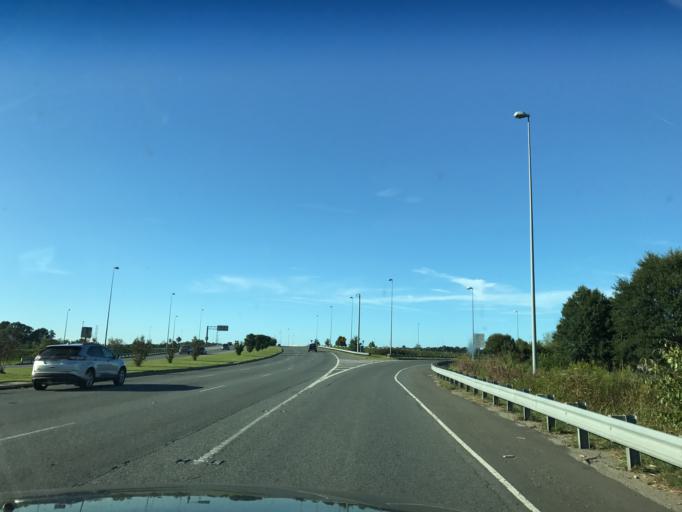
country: US
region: Virginia
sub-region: City of Chesapeake
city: Chesapeake
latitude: 36.7705
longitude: -76.2526
